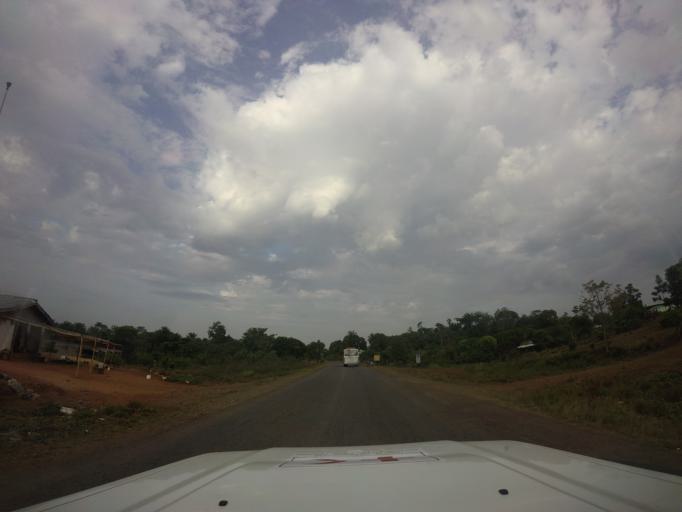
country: LR
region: Bomi
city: Tubmanburg
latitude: 6.7320
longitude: -10.9957
